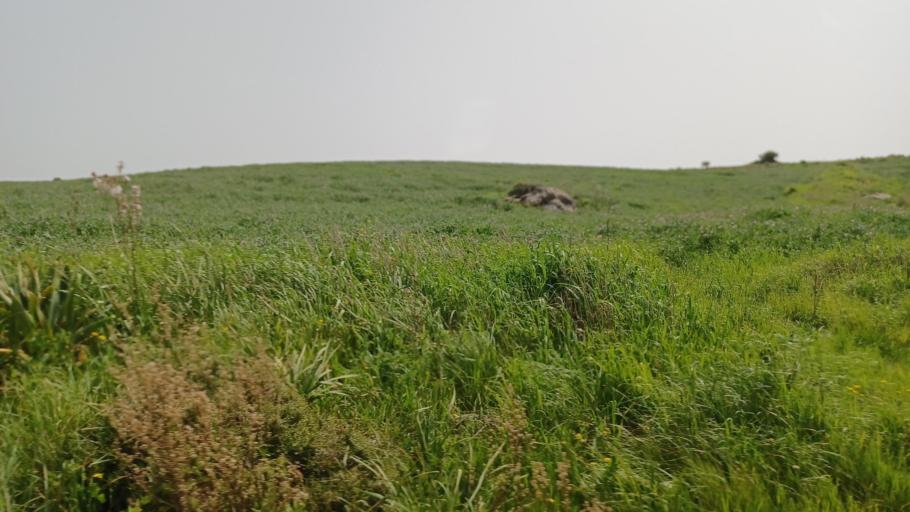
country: CY
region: Pafos
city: Polis
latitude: 34.9846
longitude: 32.3878
